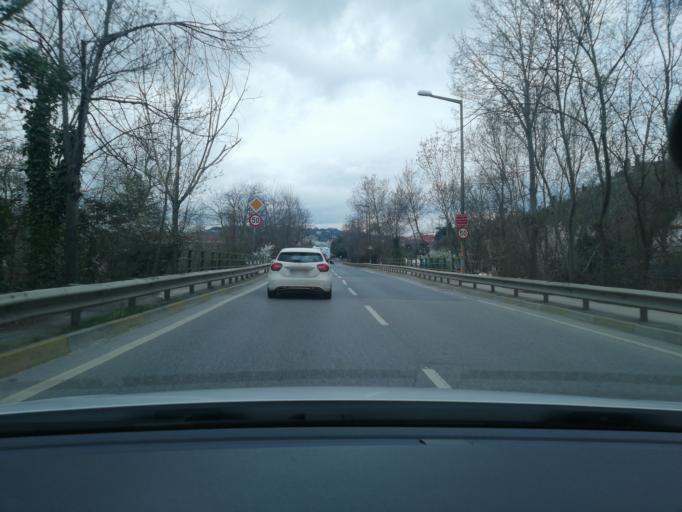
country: TR
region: Istanbul
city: UEskuedar
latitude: 41.0804
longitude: 29.0755
